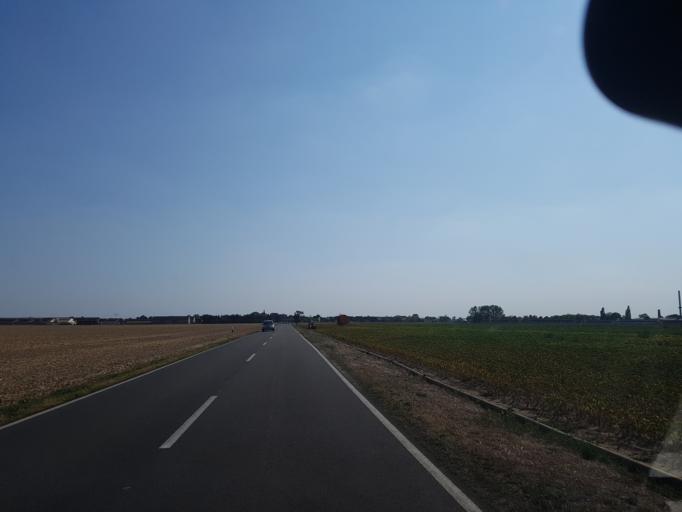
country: DE
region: Saxony-Anhalt
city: Prettin
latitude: 51.6558
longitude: 12.9872
